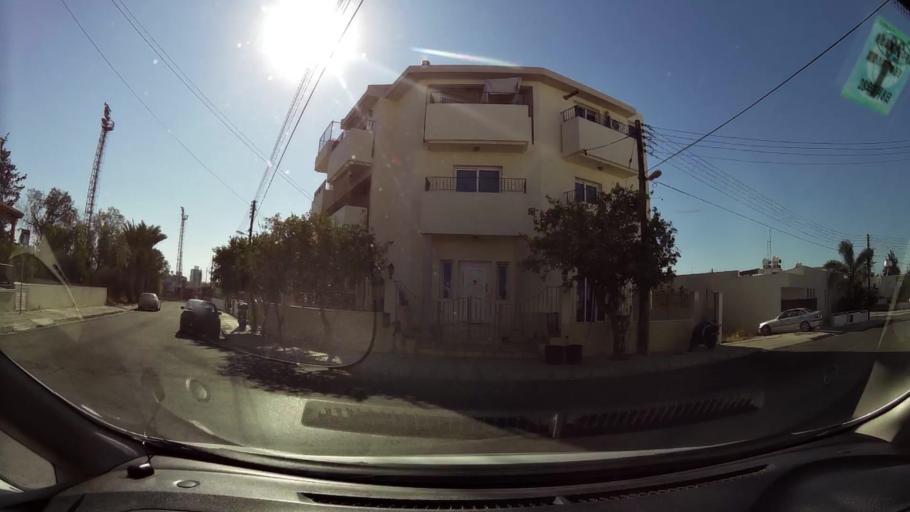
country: CY
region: Larnaka
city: Larnaca
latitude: 34.9343
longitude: 33.6179
